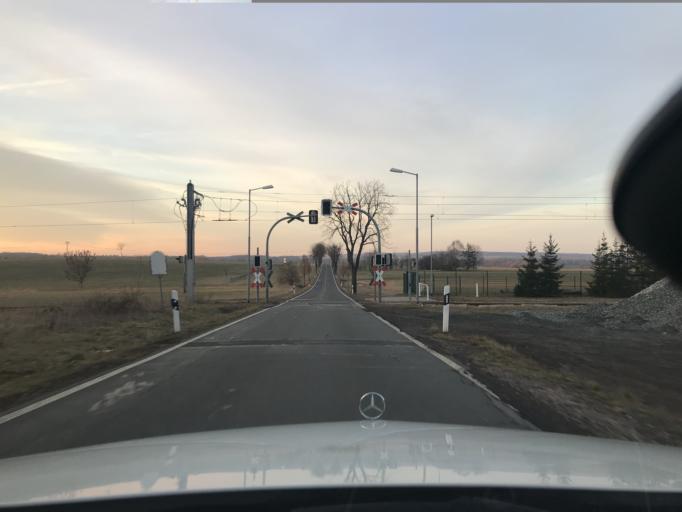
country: DE
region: Thuringia
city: Emleben
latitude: 50.9110
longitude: 10.6528
